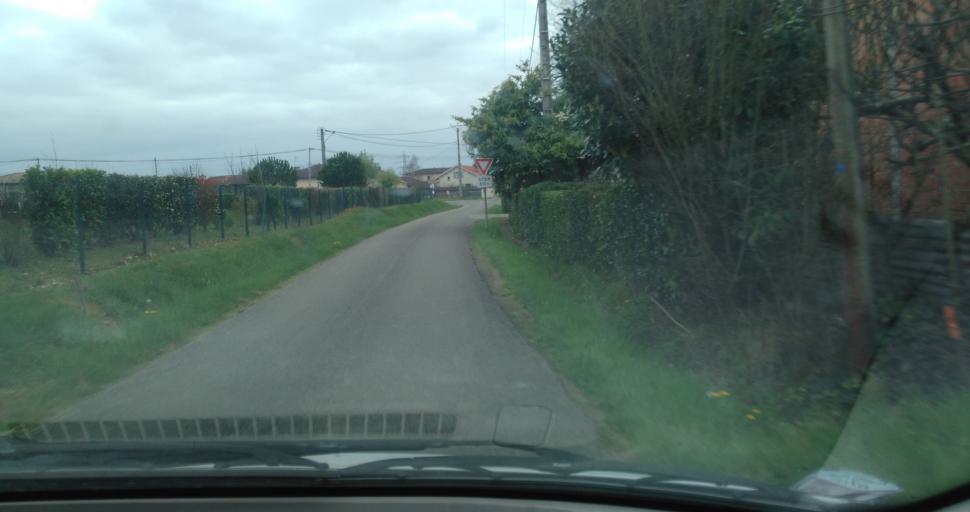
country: FR
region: Midi-Pyrenees
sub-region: Departement du Tarn-et-Garonne
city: Montbeton
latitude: 44.0081
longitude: 1.3194
